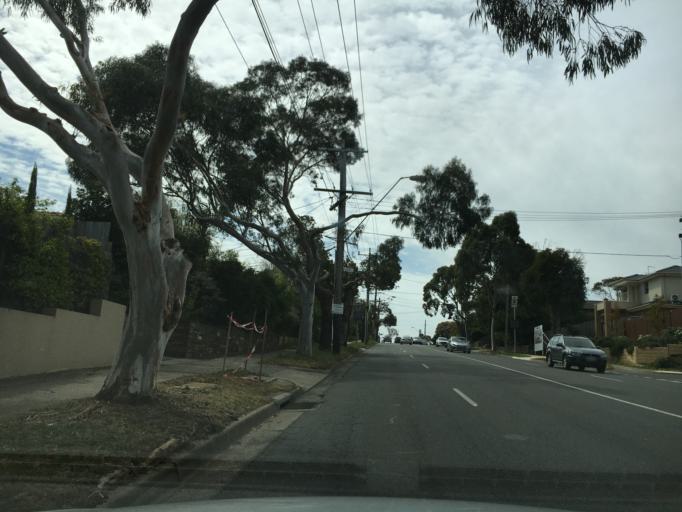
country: AU
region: Victoria
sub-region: Monash
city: Chadstone
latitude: -37.8910
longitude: 145.1073
